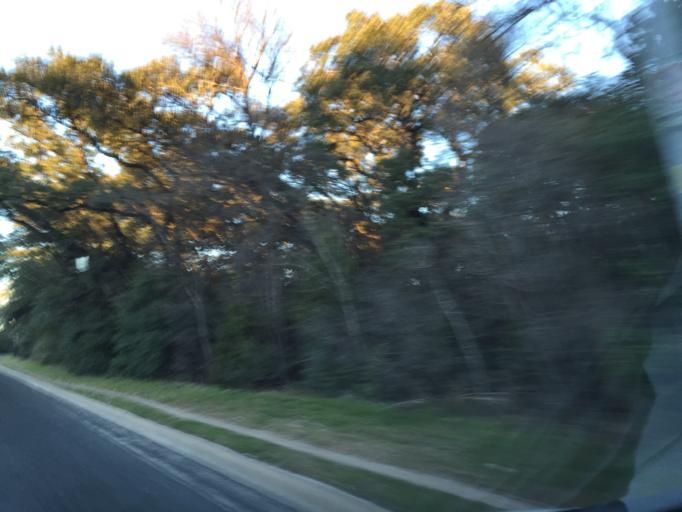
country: US
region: Texas
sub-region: Williamson County
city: Jollyville
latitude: 30.3957
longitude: -97.7399
